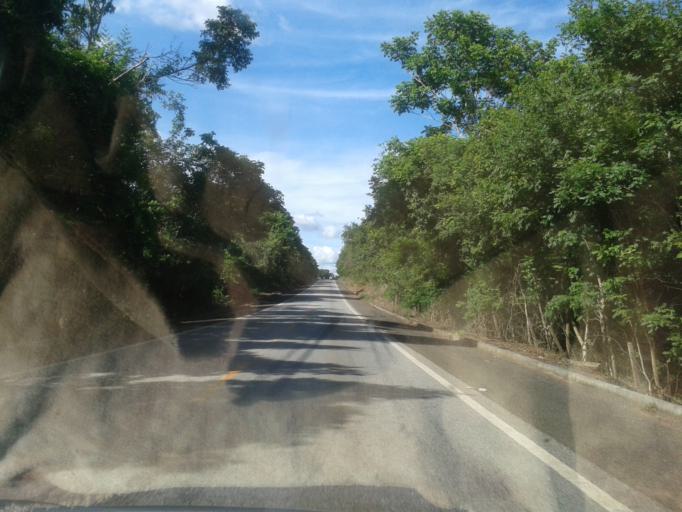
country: BR
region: Goias
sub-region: Mozarlandia
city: Mozarlandia
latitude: -14.9472
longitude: -50.5783
